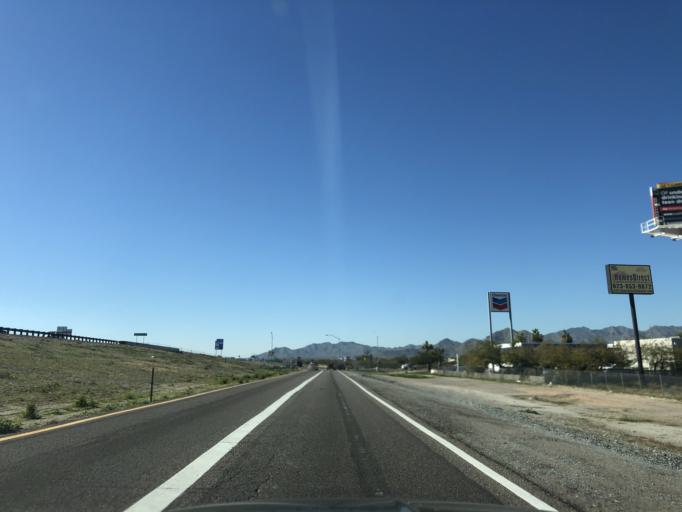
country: US
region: Arizona
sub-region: Maricopa County
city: Citrus Park
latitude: 33.4630
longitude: -112.4770
